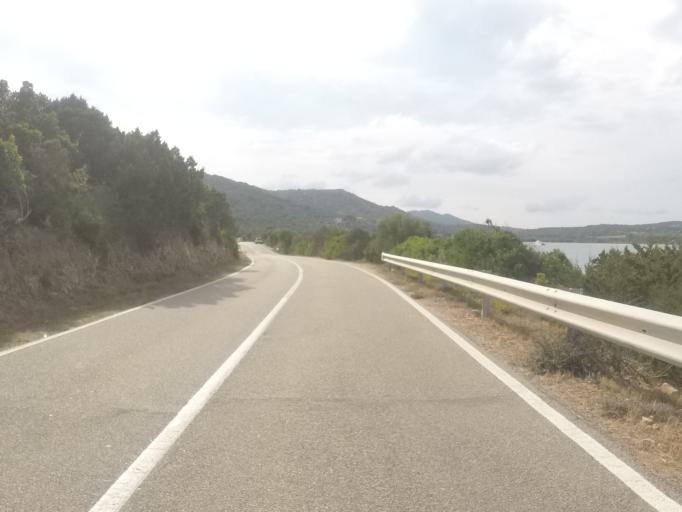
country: IT
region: Sardinia
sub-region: Provincia di Olbia-Tempio
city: Palau
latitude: 41.1560
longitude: 9.4146
